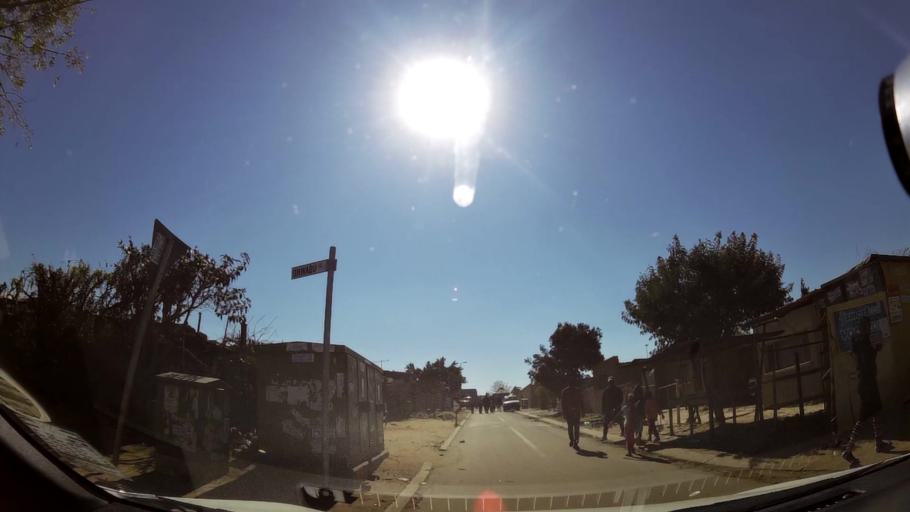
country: ZA
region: Gauteng
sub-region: City of Johannesburg Metropolitan Municipality
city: Diepsloot
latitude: -25.9171
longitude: 28.0899
